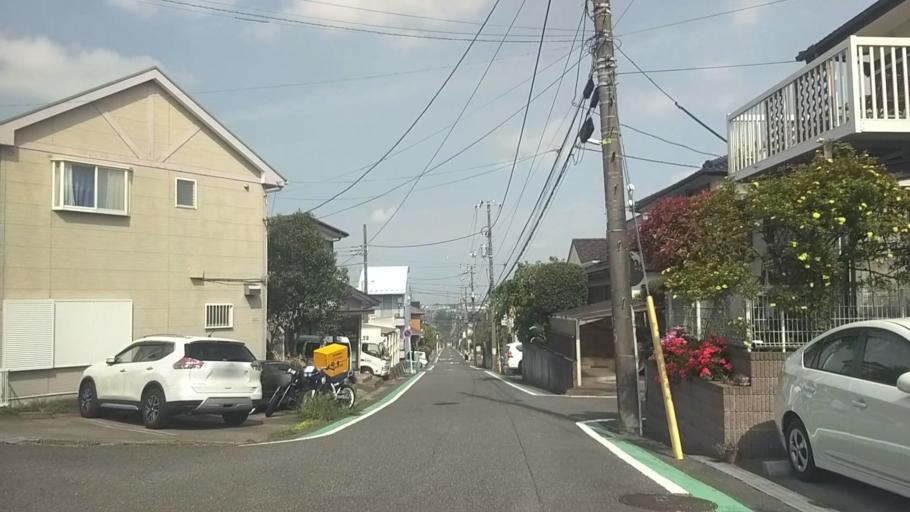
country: JP
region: Kanagawa
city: Yokohama
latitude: 35.3704
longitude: 139.6177
